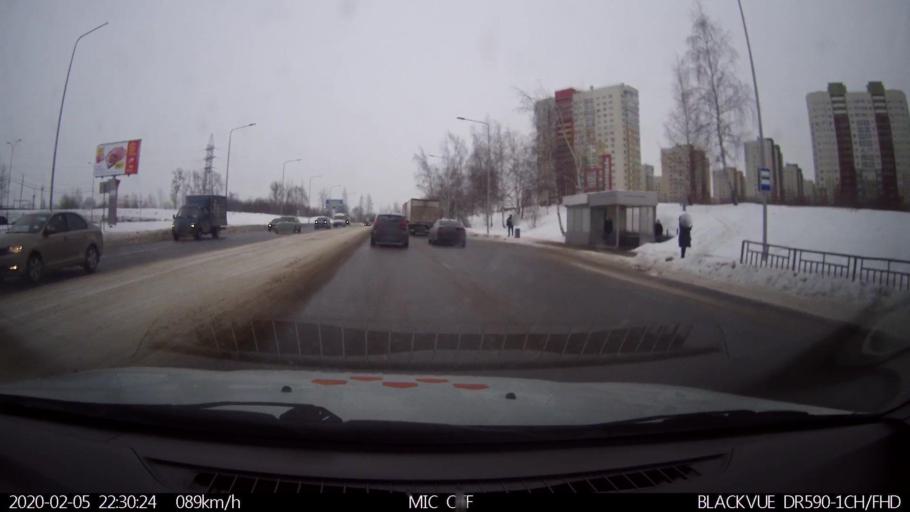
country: RU
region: Nizjnij Novgorod
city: Imeni Stepana Razina
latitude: 54.7431
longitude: 44.1606
